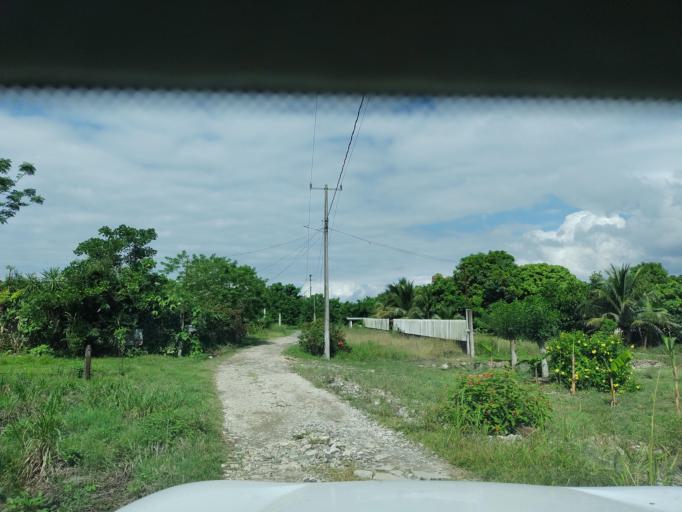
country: MX
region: Veracruz
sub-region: Atzalan
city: Colonias Pedernales
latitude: 20.0421
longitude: -97.0767
